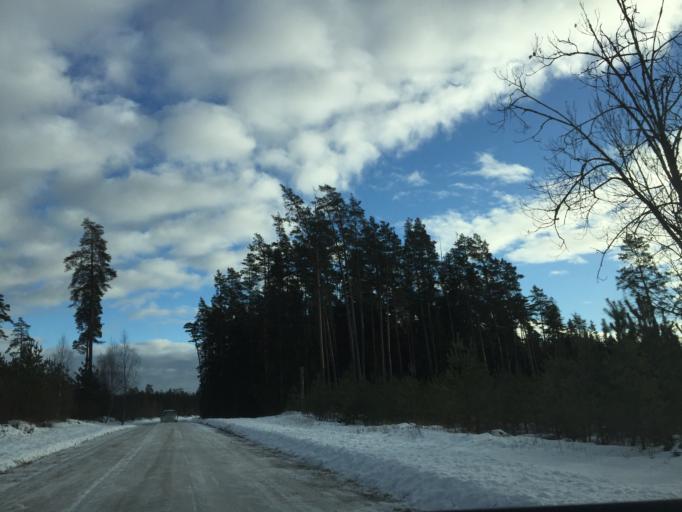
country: LV
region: Lielvarde
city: Lielvarde
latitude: 56.5666
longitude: 24.8287
